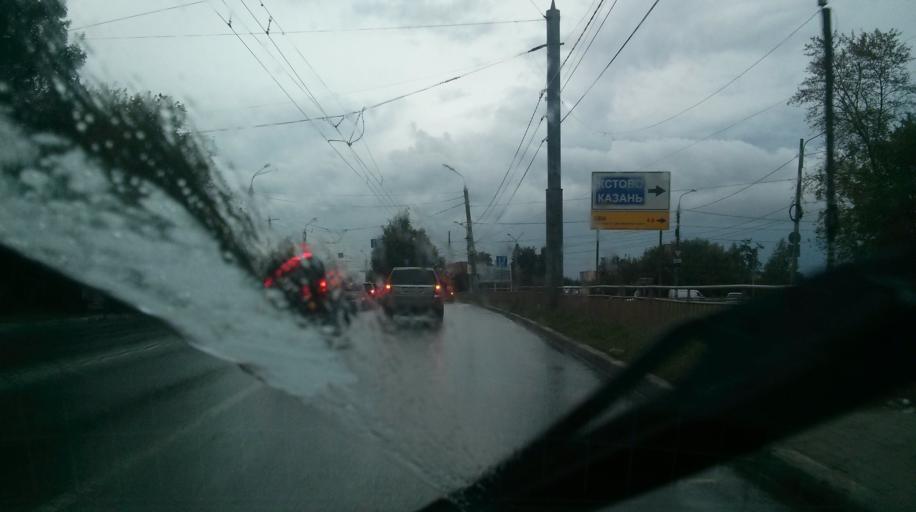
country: RU
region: Nizjnij Novgorod
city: Nizhniy Novgorod
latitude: 56.2992
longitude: 44.0327
